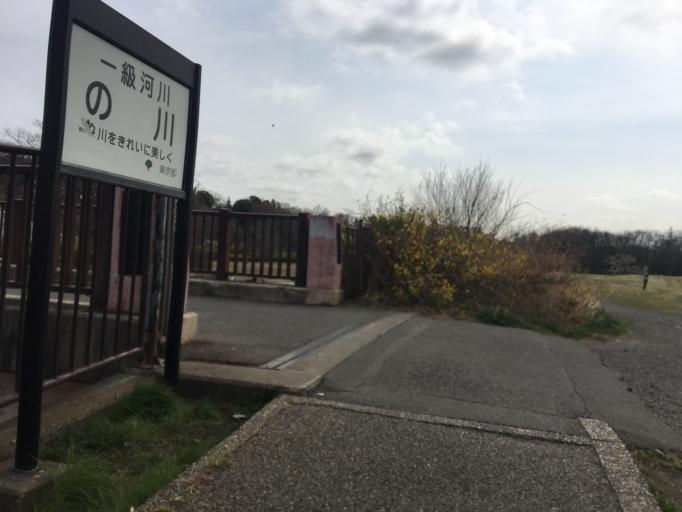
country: JP
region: Tokyo
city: Kokubunji
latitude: 35.6924
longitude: 139.5145
